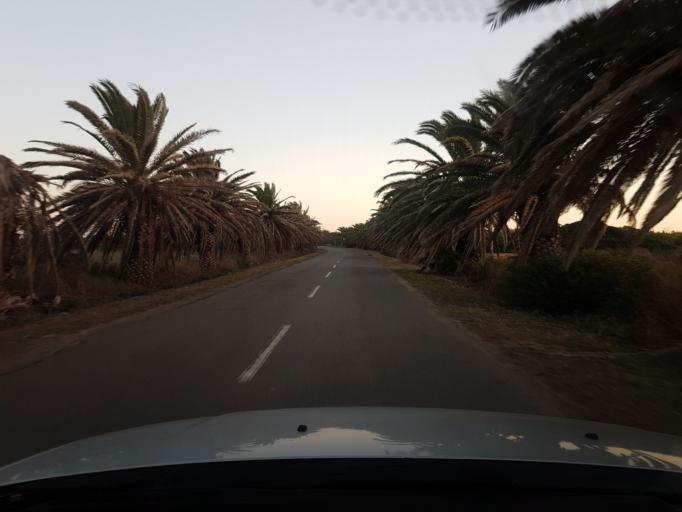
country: IT
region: Sardinia
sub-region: Provincia di Oristano
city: Riola Sardo
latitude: 40.0389
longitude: 8.4008
